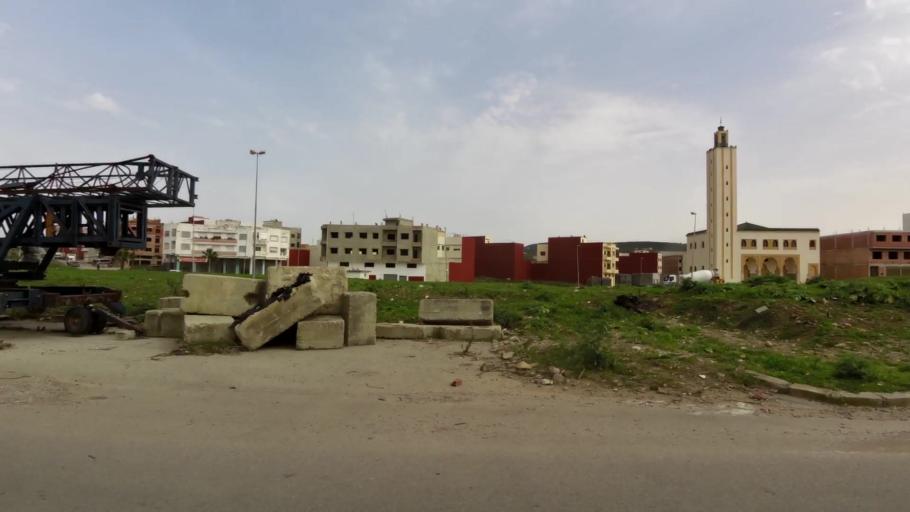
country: MA
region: Tanger-Tetouan
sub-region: Tanger-Assilah
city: Boukhalef
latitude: 35.7115
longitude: -5.8946
